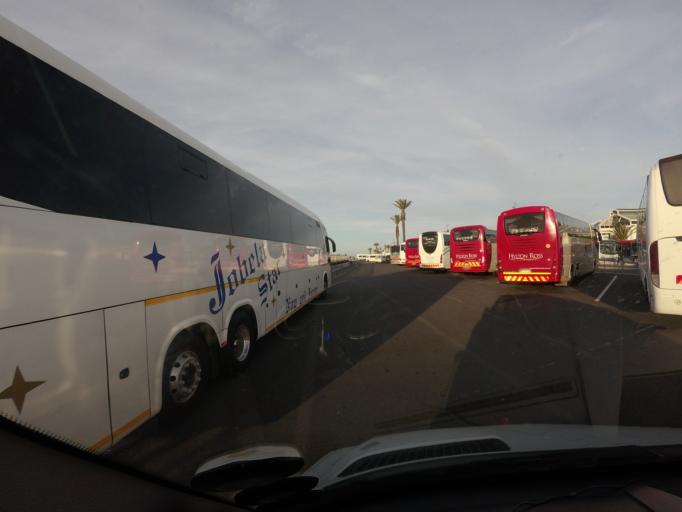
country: ZA
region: Western Cape
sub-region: City of Cape Town
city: Cape Town
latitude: -33.9021
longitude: 18.4203
